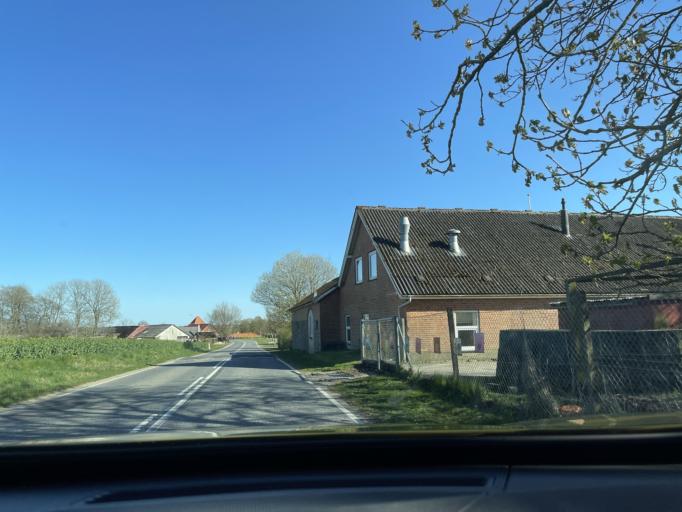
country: DK
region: Central Jutland
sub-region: Silkeborg Kommune
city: Kjellerup
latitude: 56.2548
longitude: 9.4218
